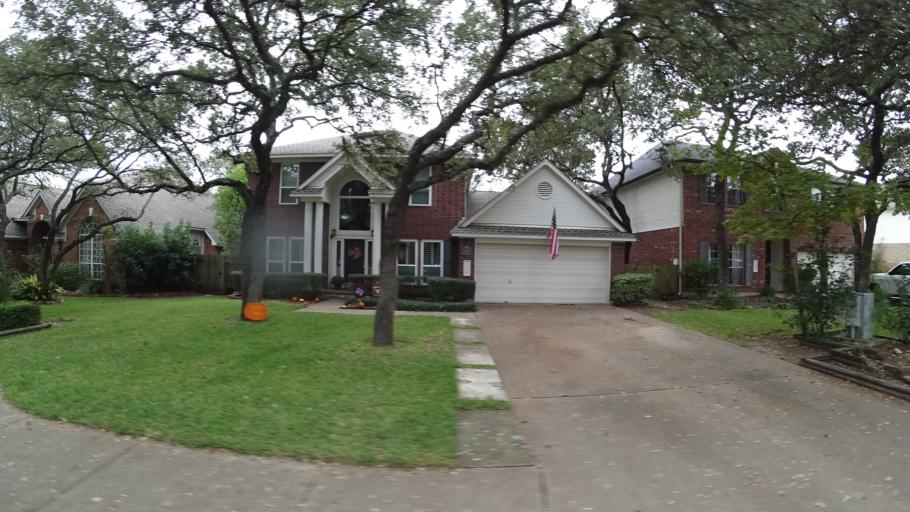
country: US
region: Texas
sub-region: Williamson County
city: Anderson Mill
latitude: 30.4424
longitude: -97.8232
